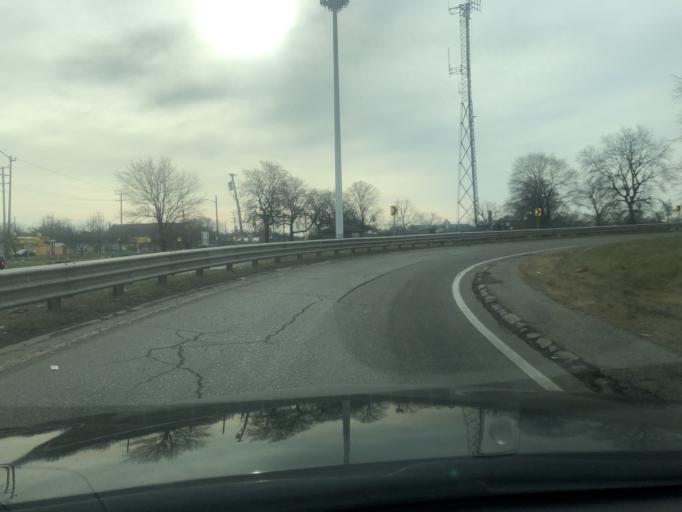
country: US
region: Michigan
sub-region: Wayne County
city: Melvindale
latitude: 42.2765
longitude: -83.1559
